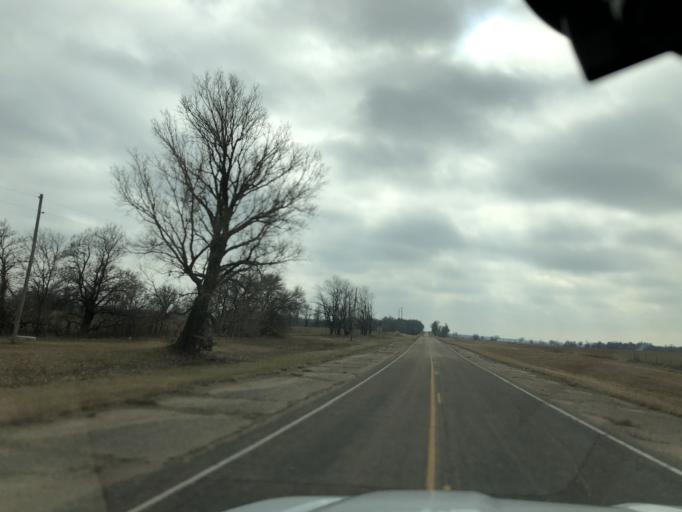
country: US
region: Kansas
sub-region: Stafford County
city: Stafford
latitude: 37.9738
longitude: -98.3992
